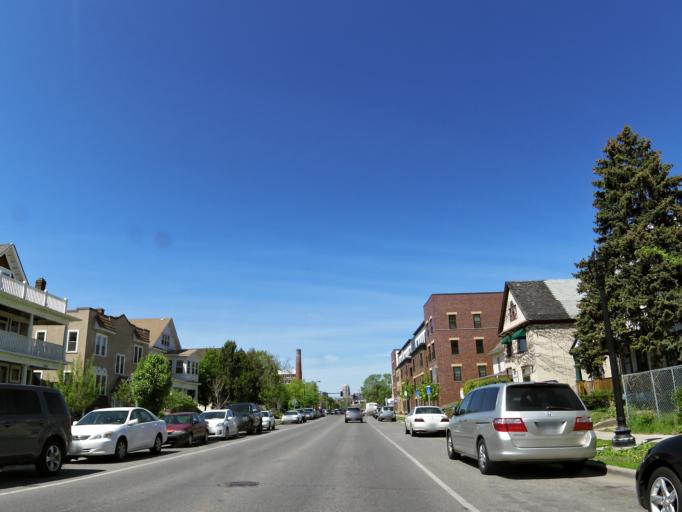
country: US
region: Minnesota
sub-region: Hennepin County
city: Minneapolis
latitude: 44.9578
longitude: -93.2625
